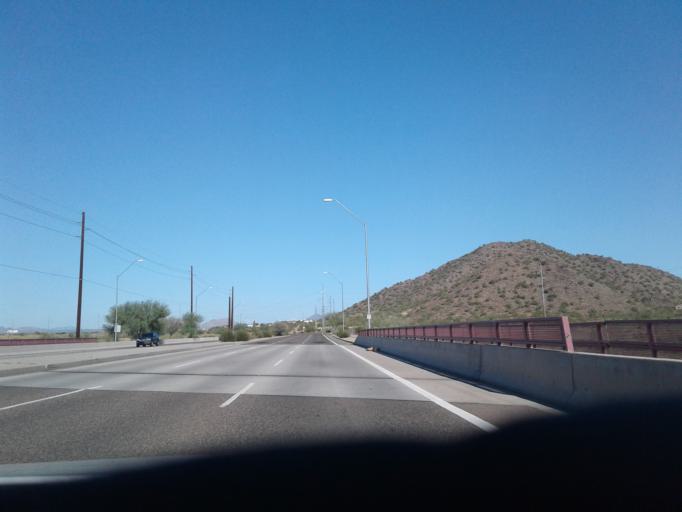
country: US
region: Arizona
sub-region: Maricopa County
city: Cave Creek
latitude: 33.6839
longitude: -112.0587
